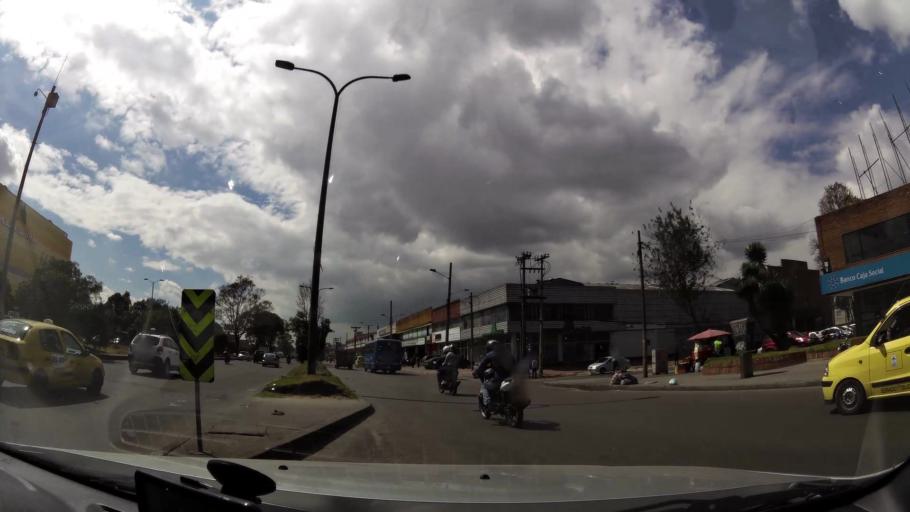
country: CO
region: Bogota D.C.
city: Bogota
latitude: 4.6332
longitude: -74.1129
